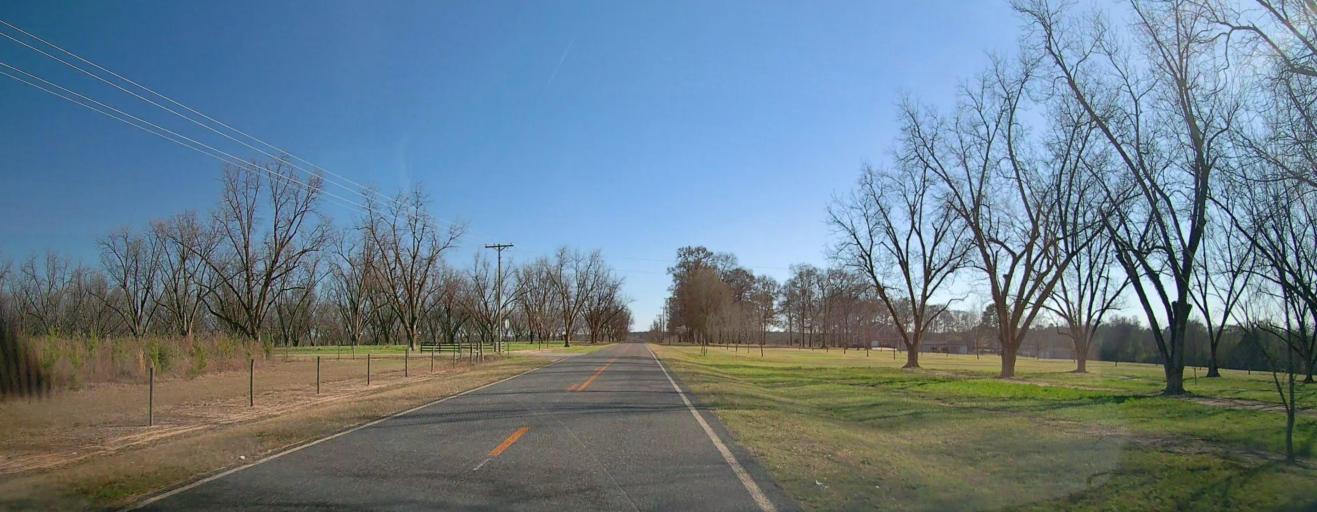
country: US
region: Georgia
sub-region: Peach County
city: Fort Valley
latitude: 32.6041
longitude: -83.8523
